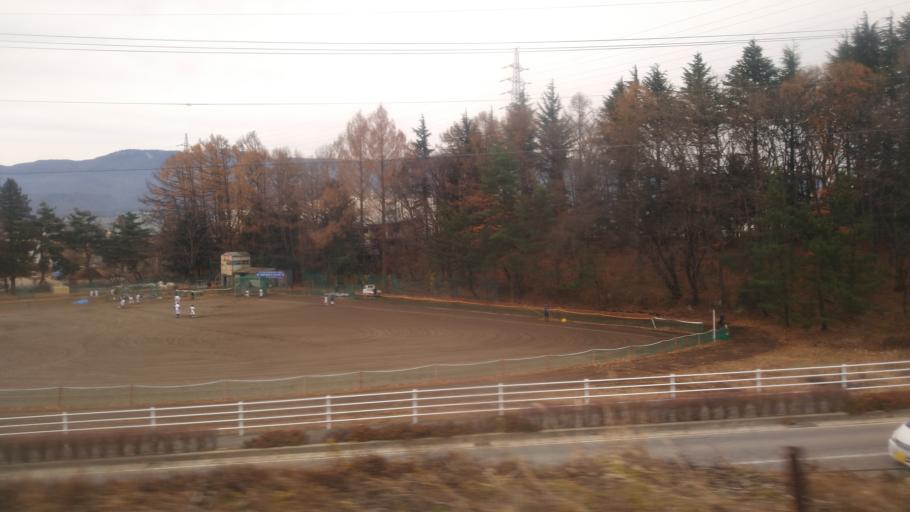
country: JP
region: Nagano
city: Shiojiri
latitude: 36.1365
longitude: 137.9490
